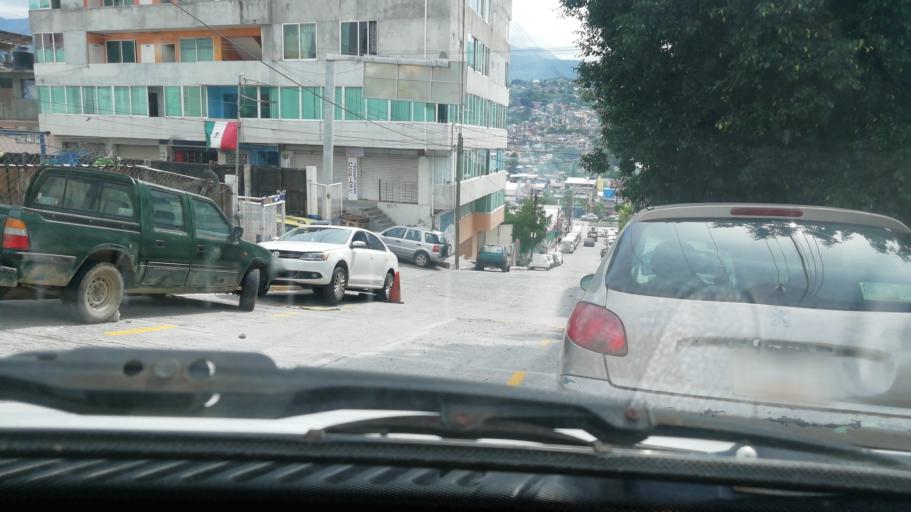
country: MX
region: Guerrero
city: Chilpancingo de los Bravos
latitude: 17.5657
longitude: -99.5079
